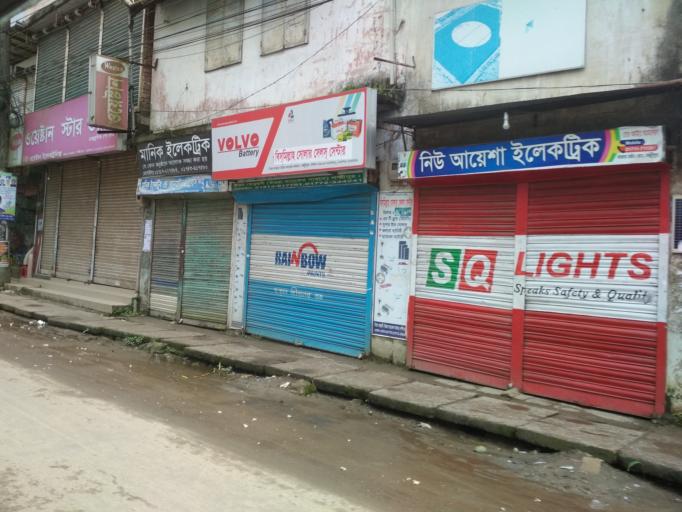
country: BD
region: Chittagong
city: Lakshmipur
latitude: 22.9435
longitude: 90.8282
